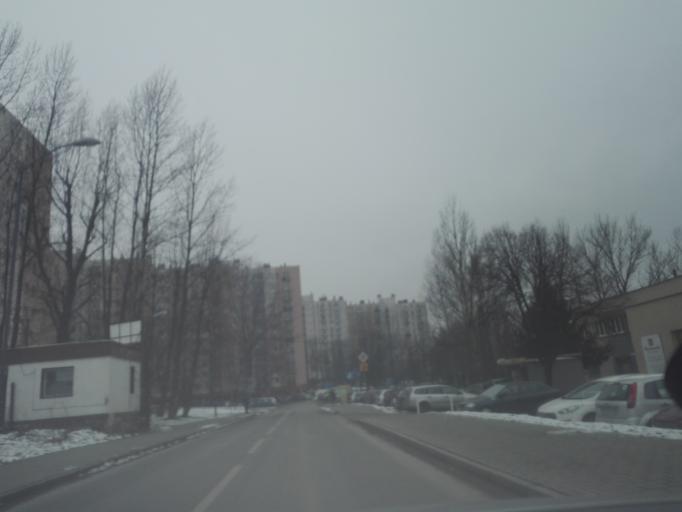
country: PL
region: Silesian Voivodeship
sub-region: Katowice
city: Katowice
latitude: 50.2489
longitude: 19.0388
